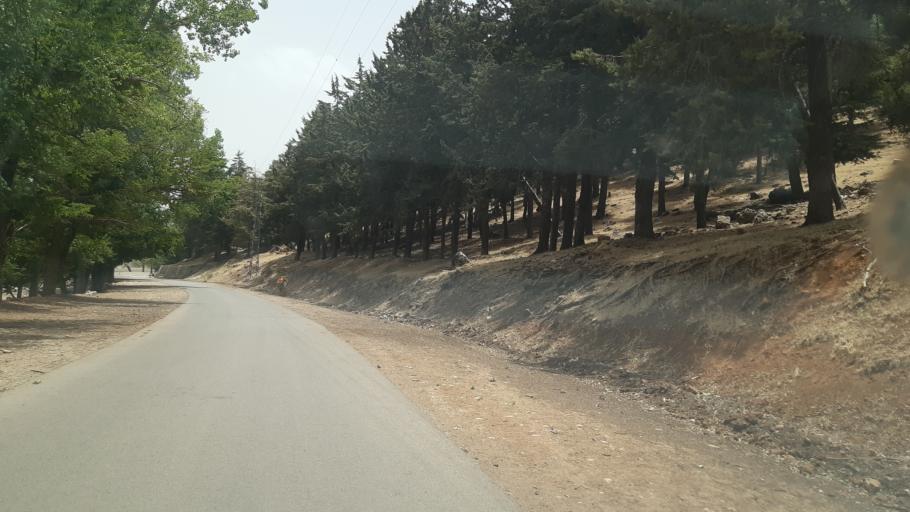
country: MA
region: Meknes-Tafilalet
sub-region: Ifrane
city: Ifrane
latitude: 33.6530
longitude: -5.0436
